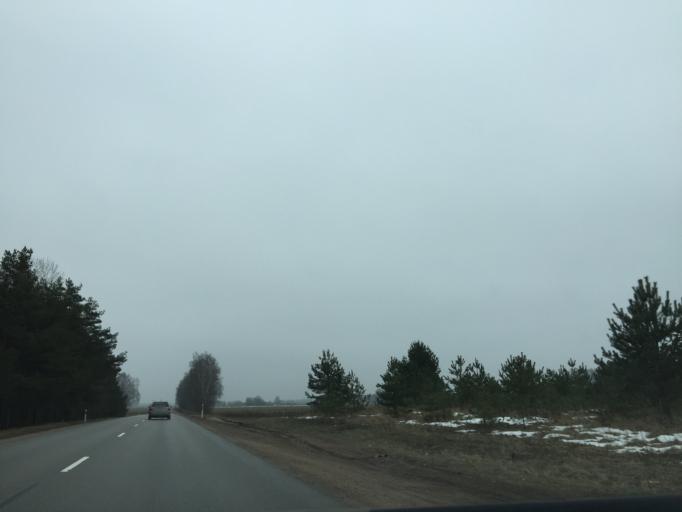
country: LV
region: Lecava
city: Iecava
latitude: 56.6018
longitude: 24.0939
